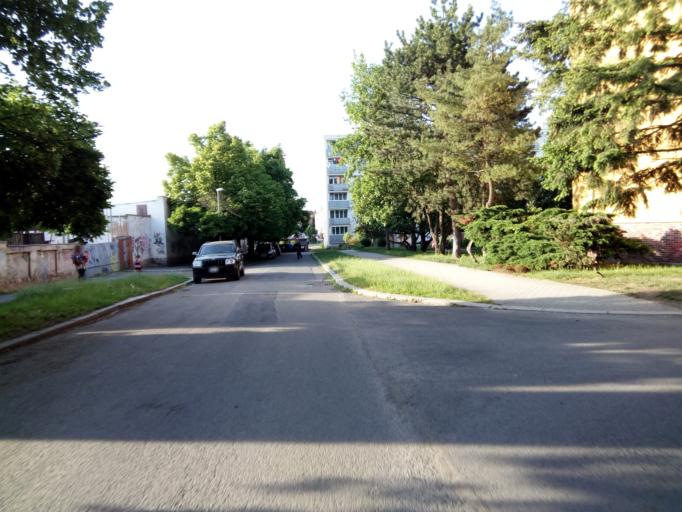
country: CZ
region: Plzensky
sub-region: Okres Plzen-Mesto
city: Pilsen
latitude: 49.7284
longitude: 13.3731
